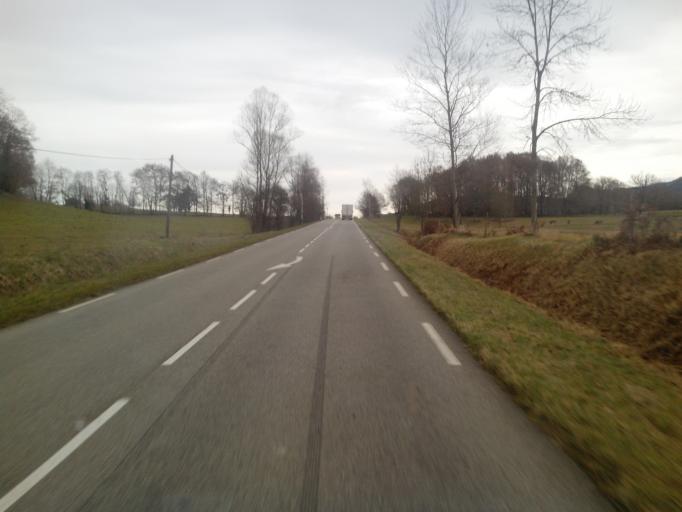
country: FR
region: Midi-Pyrenees
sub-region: Departement de l'Ariege
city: Montjoie-en-Couserans
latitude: 42.9963
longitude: 1.3067
